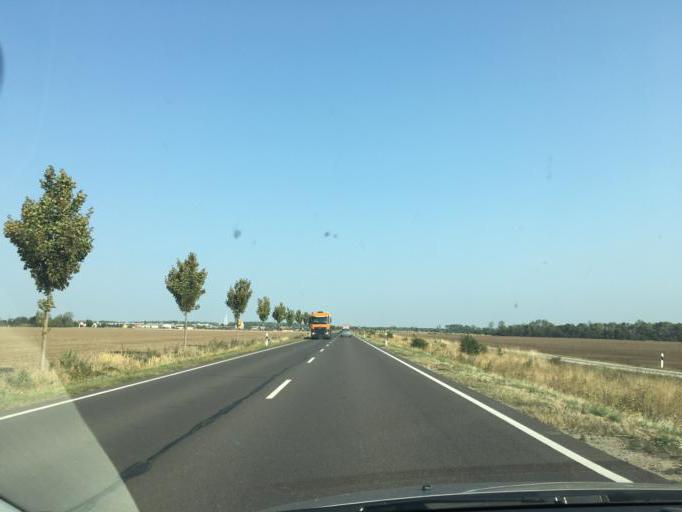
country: DE
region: Saxony-Anhalt
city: Schonebeck
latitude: 51.9997
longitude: 11.7739
